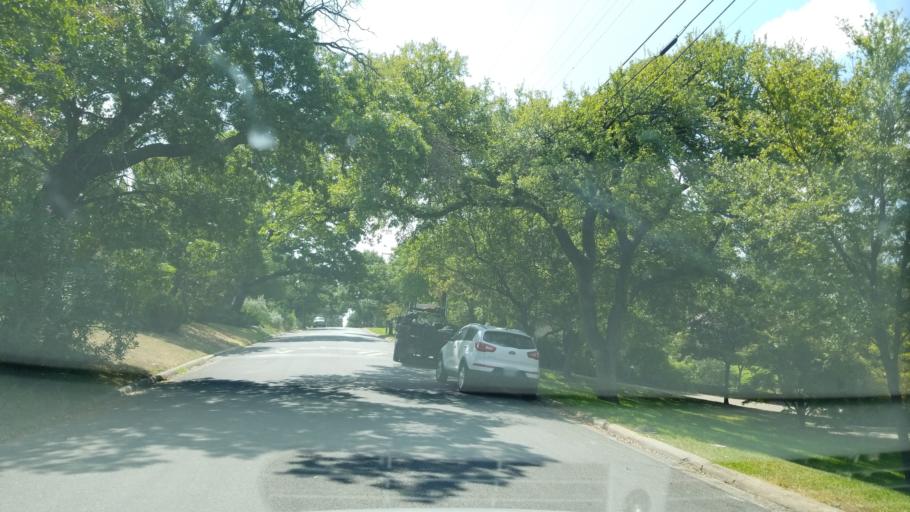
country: US
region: Texas
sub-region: Dallas County
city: Cockrell Hill
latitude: 32.7539
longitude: -96.8546
